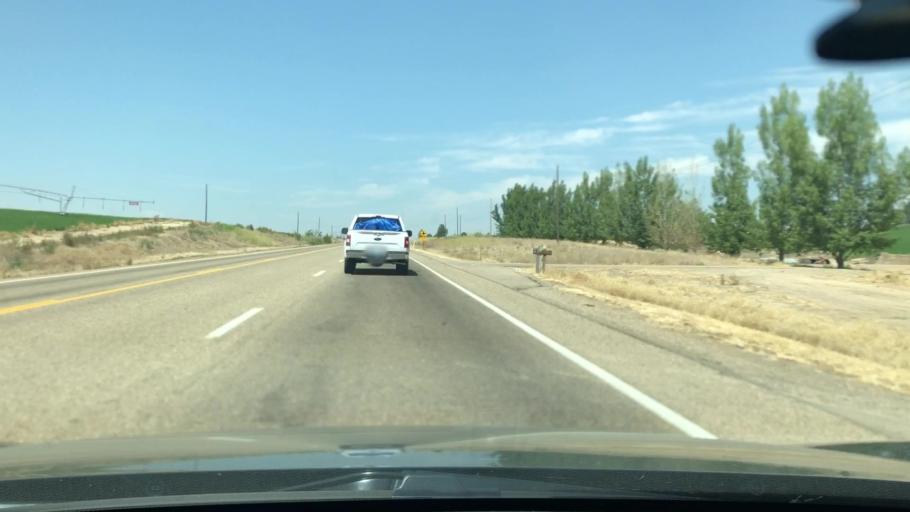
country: US
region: Idaho
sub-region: Canyon County
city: Parma
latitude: 43.8187
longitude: -116.9544
